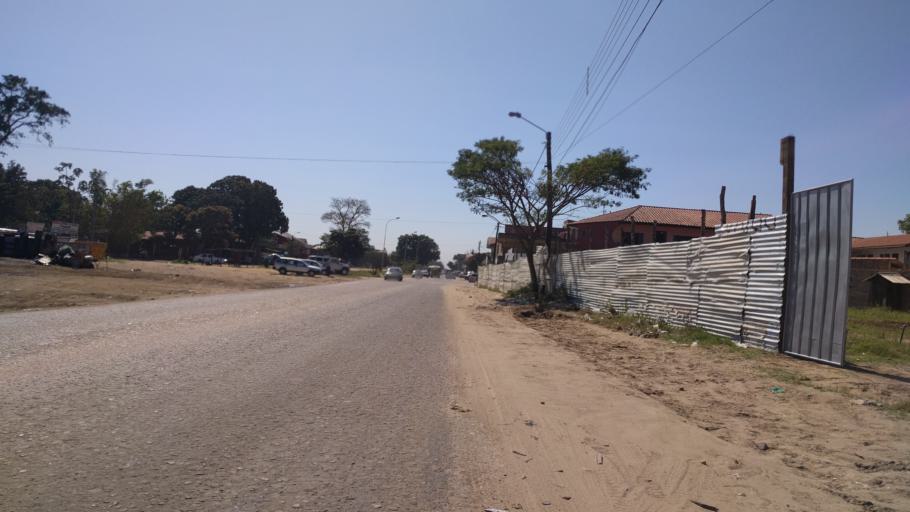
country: BO
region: Santa Cruz
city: Santa Cruz de la Sierra
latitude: -17.8234
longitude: -63.2321
